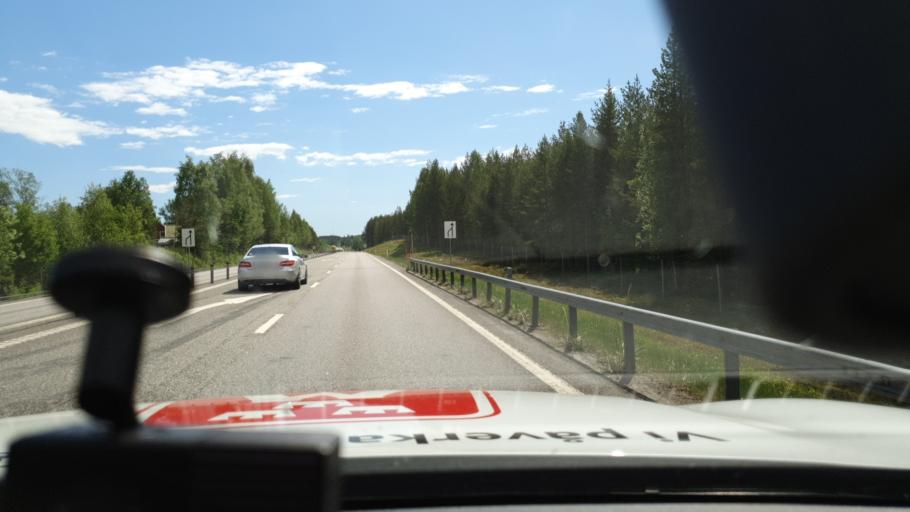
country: SE
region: Norrbotten
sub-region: Pitea Kommun
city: Pitea
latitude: 65.2690
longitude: 21.4576
